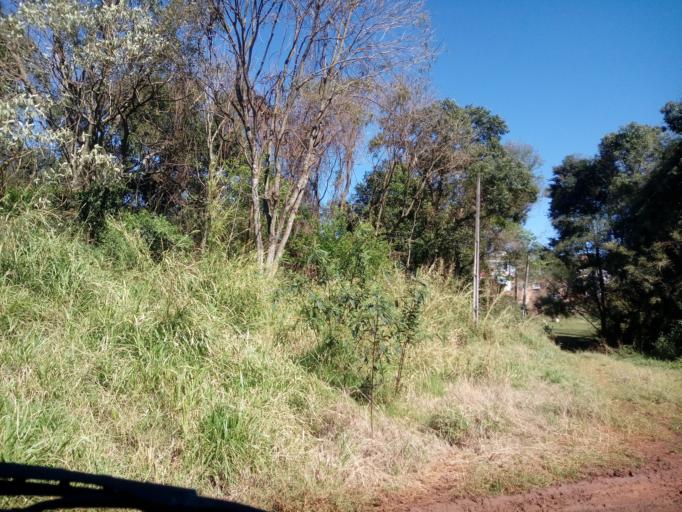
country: BR
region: Santa Catarina
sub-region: Chapeco
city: Chapeco
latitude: -27.0896
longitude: -52.6834
